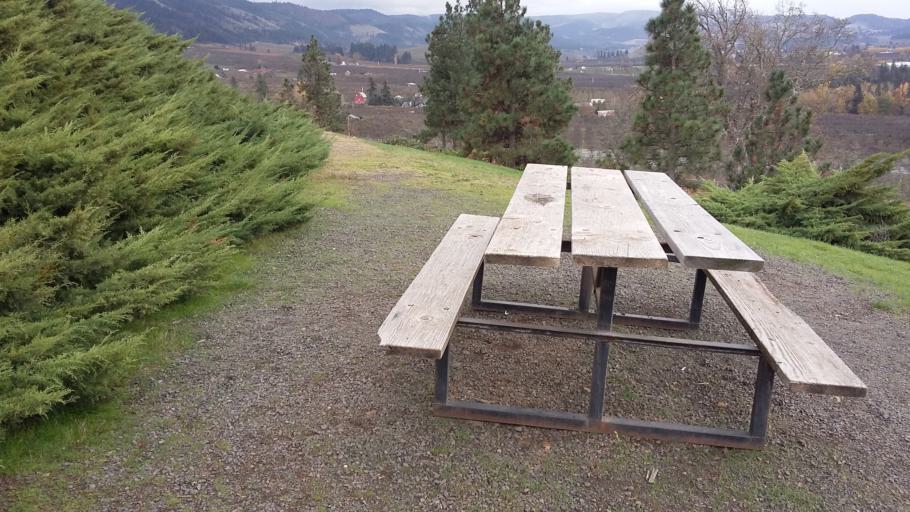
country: US
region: Oregon
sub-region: Hood River County
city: Hood River
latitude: 45.6872
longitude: -121.4999
